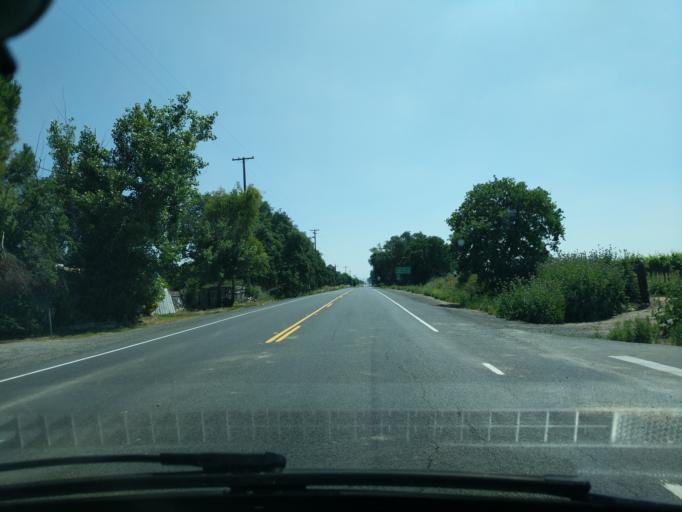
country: US
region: California
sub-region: San Joaquin County
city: Linden
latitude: 37.9300
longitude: -120.9980
